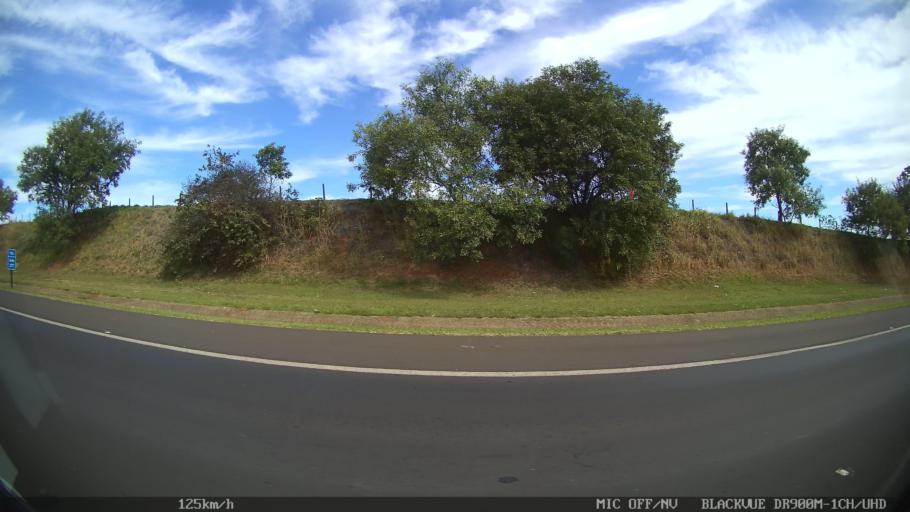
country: BR
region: Sao Paulo
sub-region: Taquaritinga
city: Taquaritinga
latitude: -21.5428
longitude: -48.5013
